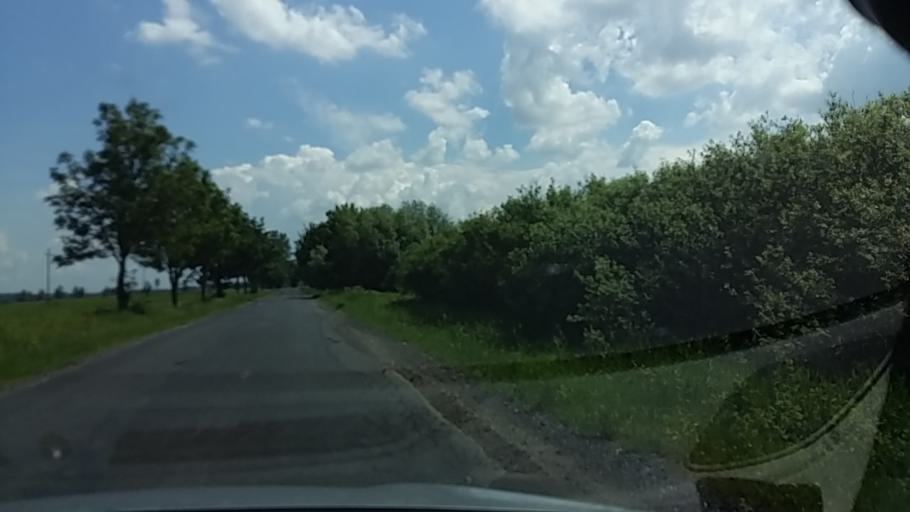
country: HU
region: Vas
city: Kormend
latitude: 46.9703
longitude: 16.5428
